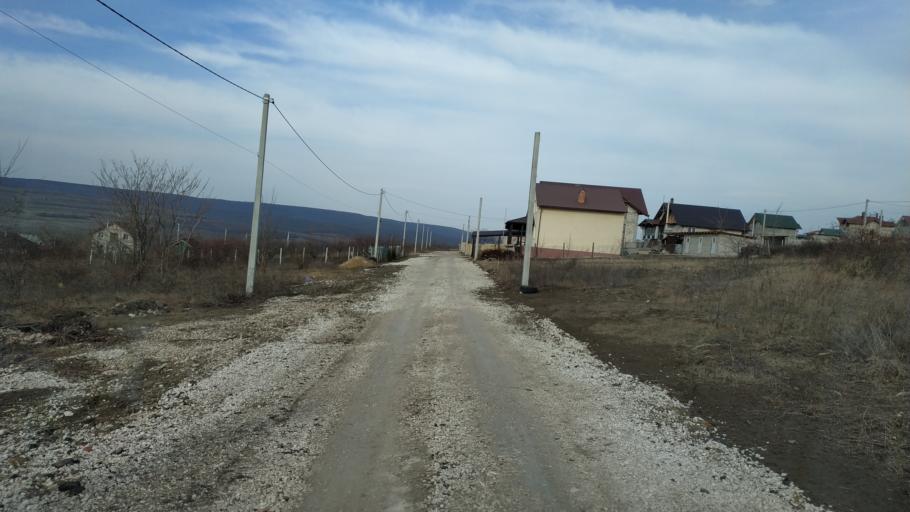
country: MD
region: Chisinau
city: Vatra
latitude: 46.9922
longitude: 28.6652
